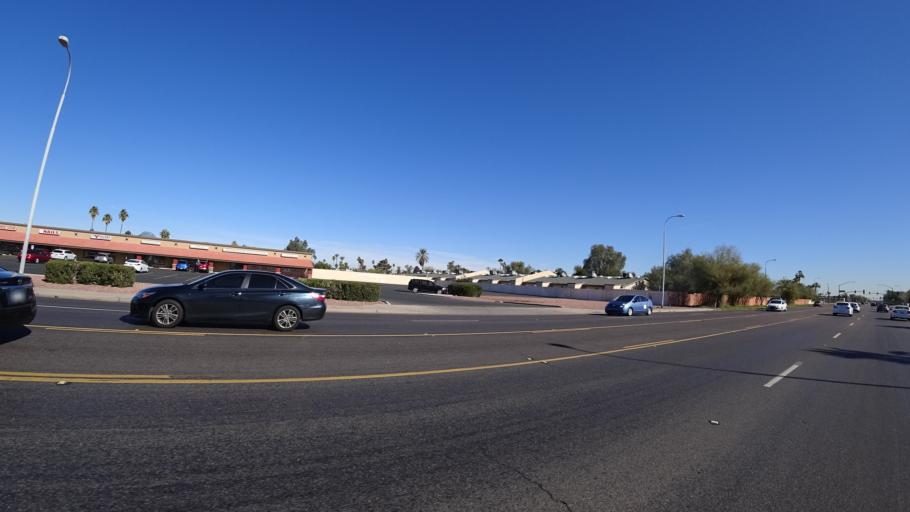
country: US
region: Arizona
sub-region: Maricopa County
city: Tolleson
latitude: 33.4936
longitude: -112.2878
